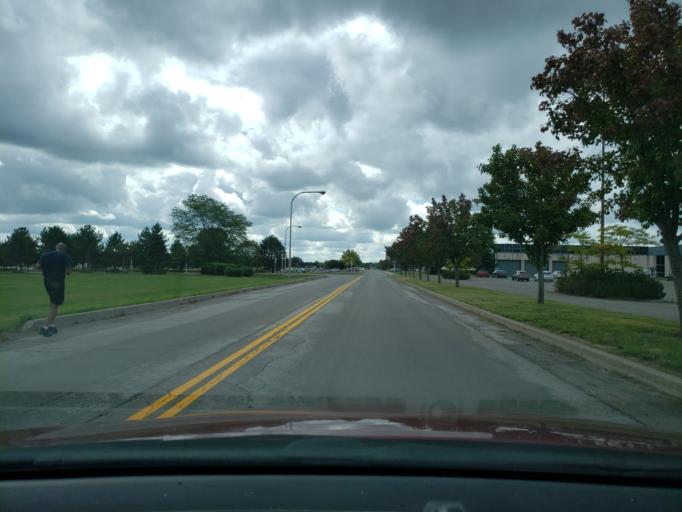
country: US
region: New York
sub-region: Monroe County
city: North Gates
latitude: 43.1558
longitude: -77.7345
